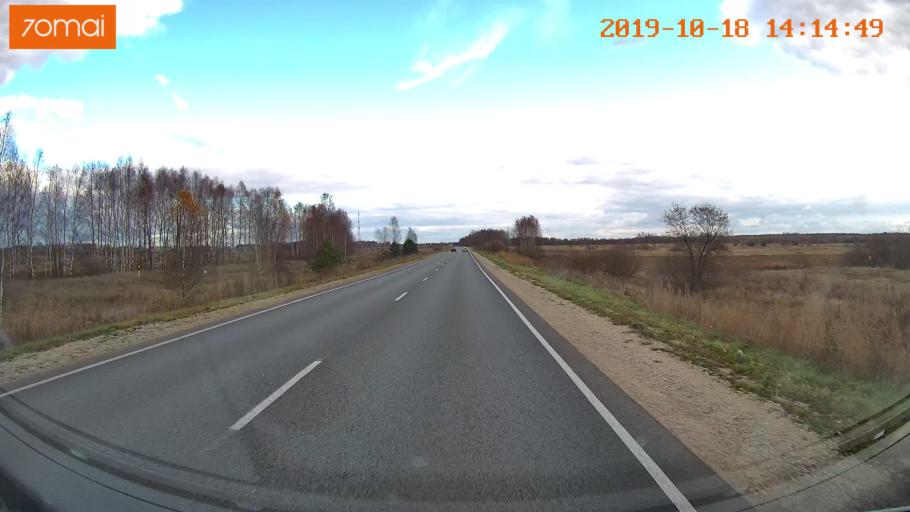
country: RU
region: Rjazan
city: Spas-Klepiki
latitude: 55.1483
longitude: 40.3035
